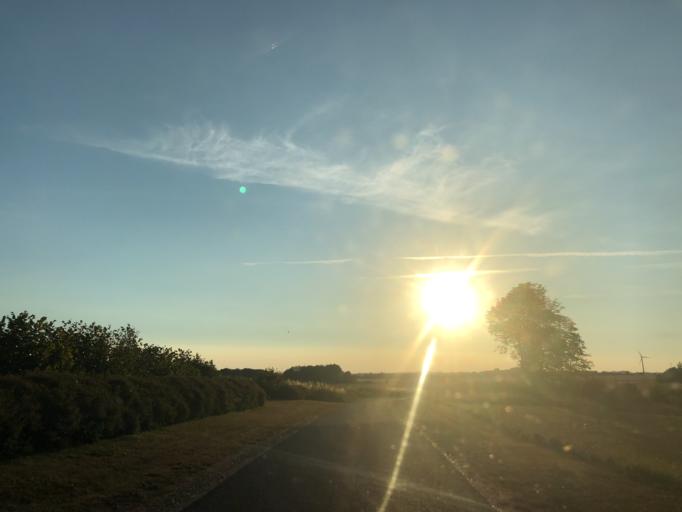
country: DK
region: Central Jutland
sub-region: Holstebro Kommune
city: Holstebro
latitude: 56.3715
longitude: 8.6722
